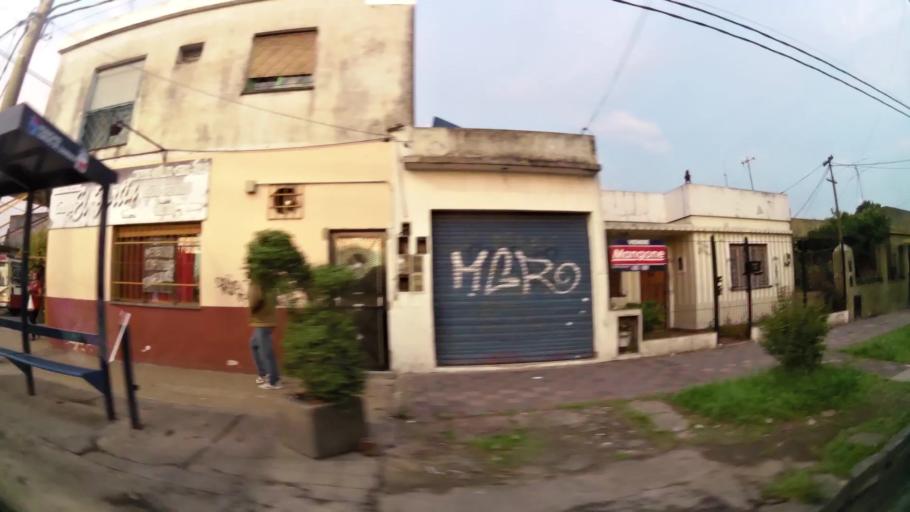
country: AR
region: Buenos Aires
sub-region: Partido de Lomas de Zamora
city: Lomas de Zamora
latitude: -34.7496
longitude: -58.3637
